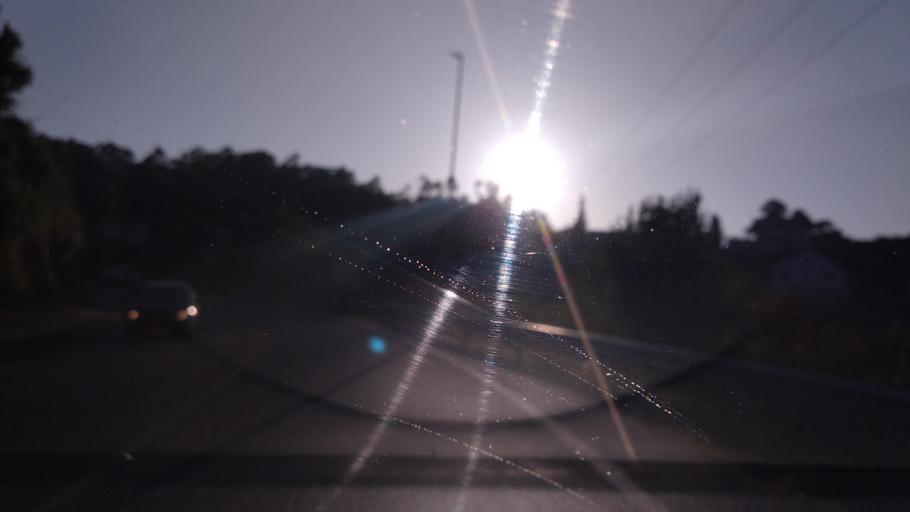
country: ES
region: Galicia
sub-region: Provincia de Pontevedra
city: Redondela
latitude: 42.3362
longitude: -8.5786
